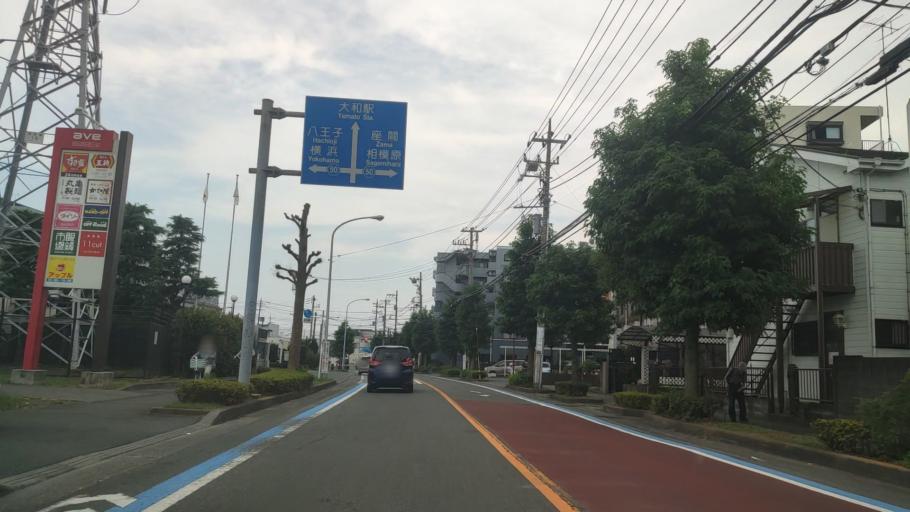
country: JP
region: Kanagawa
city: Minami-rinkan
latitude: 35.5026
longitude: 139.4494
